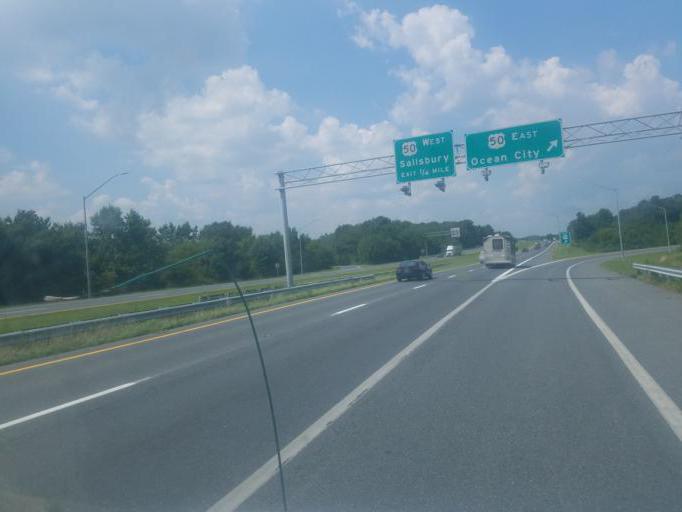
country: US
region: Maryland
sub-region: Worcester County
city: Berlin
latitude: 38.3384
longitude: -75.2122
